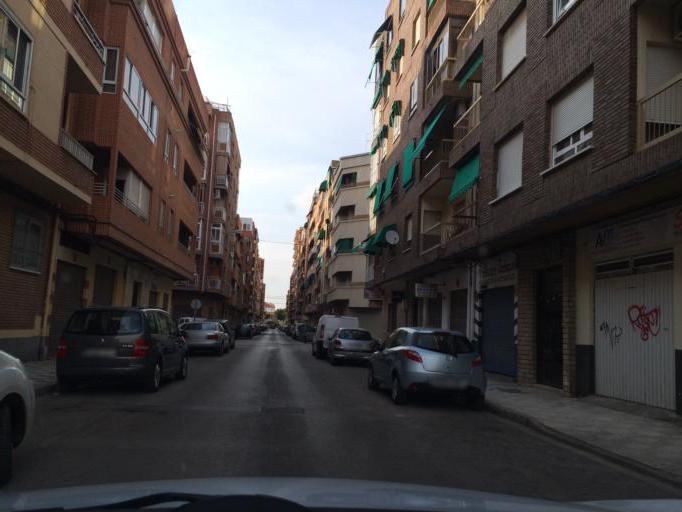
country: ES
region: Castille-La Mancha
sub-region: Provincia de Albacete
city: Albacete
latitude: 38.9886
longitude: -1.8661
